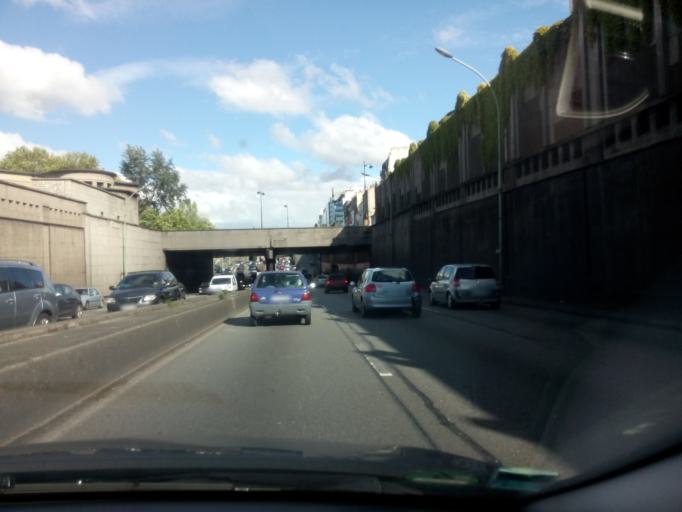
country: FR
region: Ile-de-France
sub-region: Departement des Hauts-de-Seine
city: Montrouge
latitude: 48.8213
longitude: 2.3195
